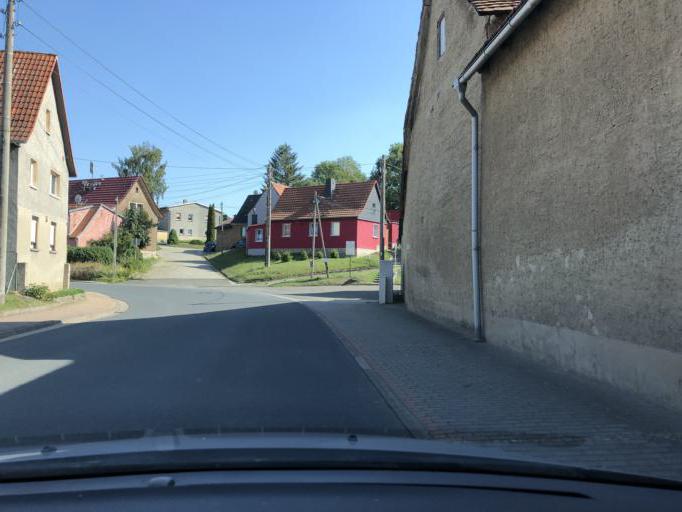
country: DE
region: Thuringia
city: Ostramondra
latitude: 51.1983
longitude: 11.3308
